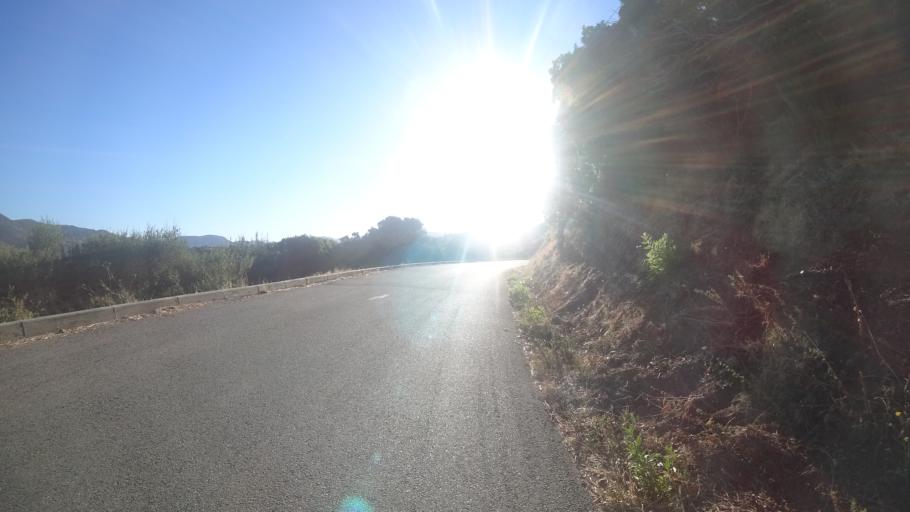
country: FR
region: Corsica
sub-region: Departement de la Corse-du-Sud
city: Alata
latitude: 41.9801
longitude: 8.6705
